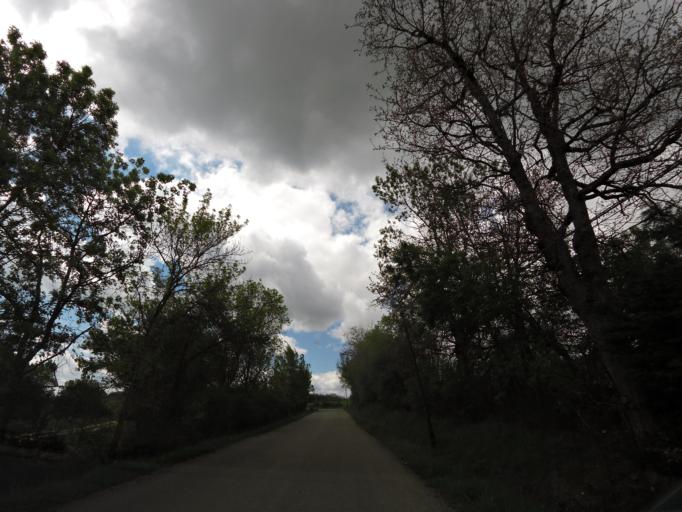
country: FR
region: Languedoc-Roussillon
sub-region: Departement de l'Aude
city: Saint-Martin-Lalande
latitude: 43.3455
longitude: 2.0665
